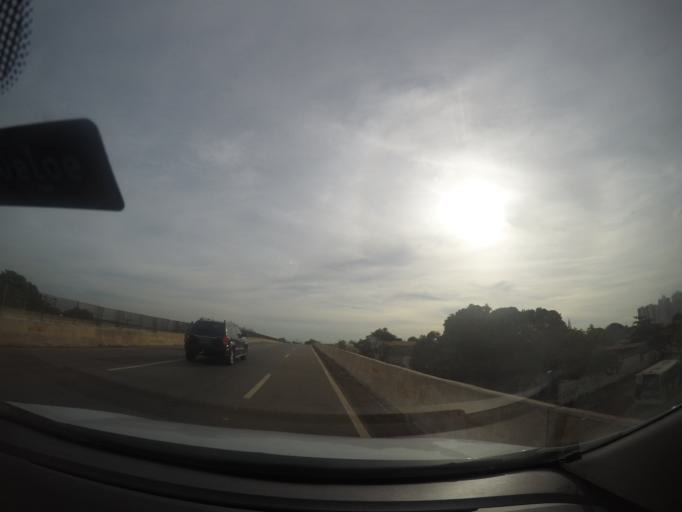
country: BR
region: Goias
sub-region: Goiania
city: Goiania
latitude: -16.7009
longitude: -49.3343
